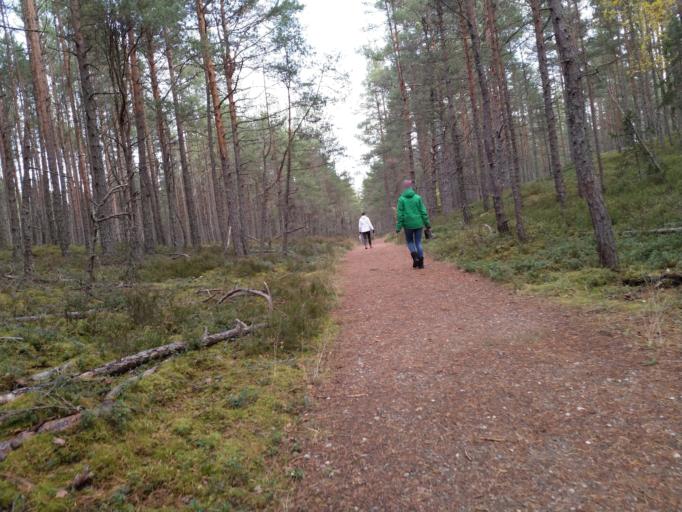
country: LV
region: Dundaga
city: Dundaga
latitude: 57.6513
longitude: 22.2596
